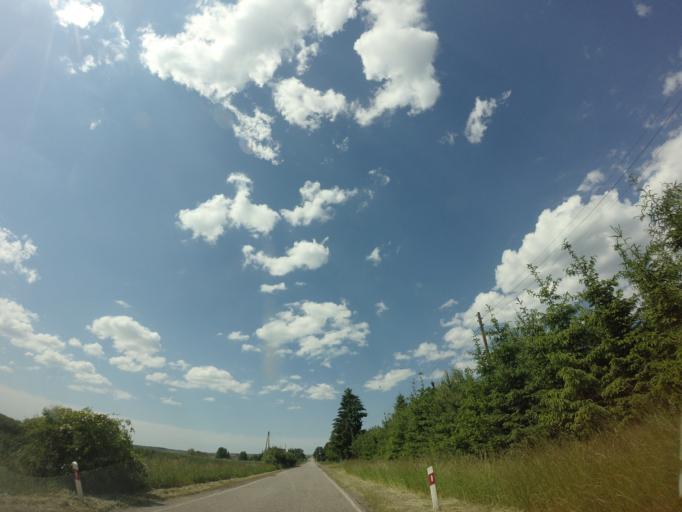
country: PL
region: West Pomeranian Voivodeship
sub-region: Powiat stargardzki
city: Dolice
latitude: 53.1617
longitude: 15.2327
